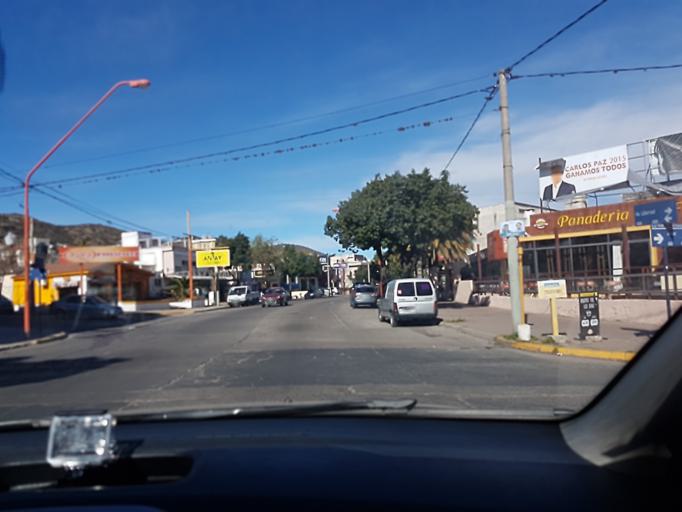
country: AR
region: Cordoba
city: Villa Carlos Paz
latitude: -31.4174
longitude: -64.4897
